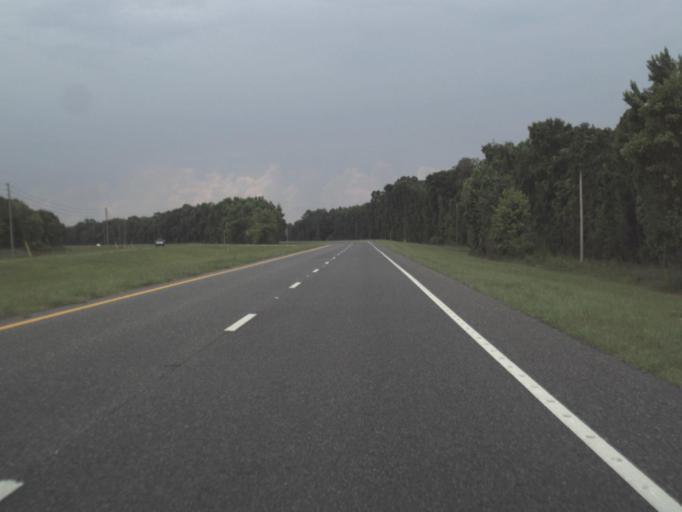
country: US
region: Florida
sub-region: Levy County
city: Inglis
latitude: 29.1904
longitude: -82.6851
